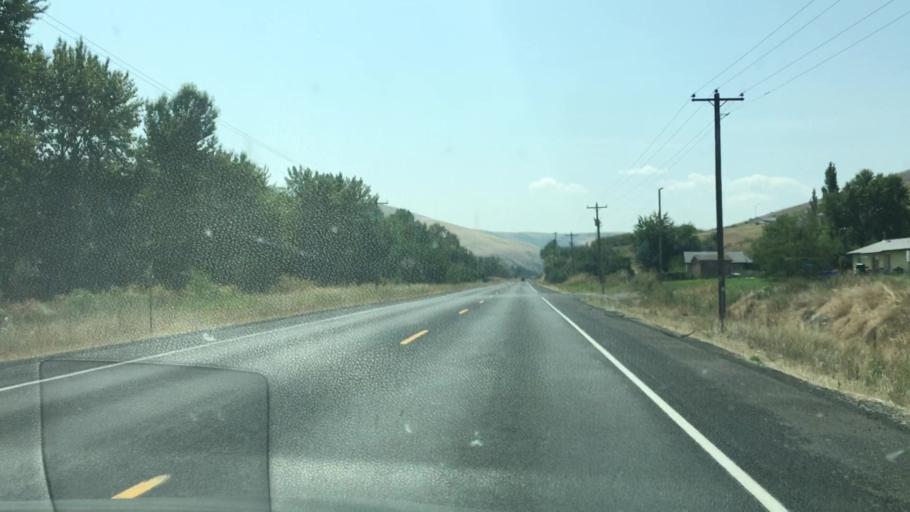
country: US
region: Idaho
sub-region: Nez Perce County
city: Lapwai
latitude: 46.3923
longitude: -116.7985
